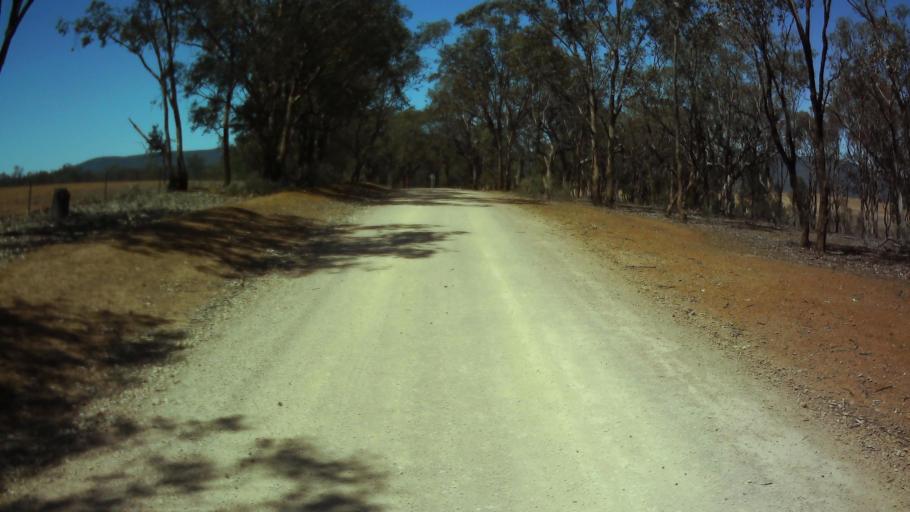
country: AU
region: New South Wales
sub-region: Weddin
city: Grenfell
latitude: -33.9320
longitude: 148.0773
